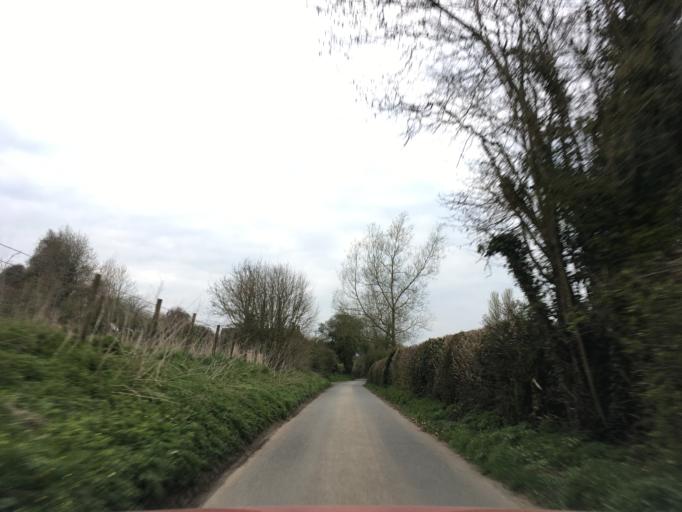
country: GB
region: England
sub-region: Gloucestershire
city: Wotton-under-Edge
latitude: 51.6051
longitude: -2.3165
